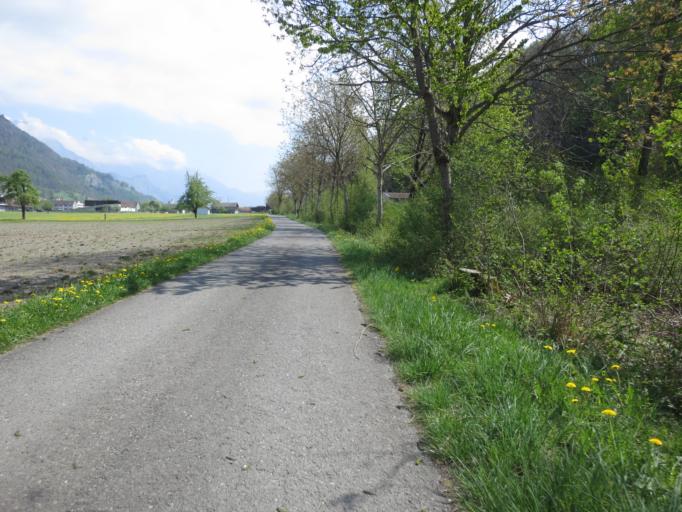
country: CH
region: Saint Gallen
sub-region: Wahlkreis Sarganserland
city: Sargans
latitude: 47.0603
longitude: 9.3958
